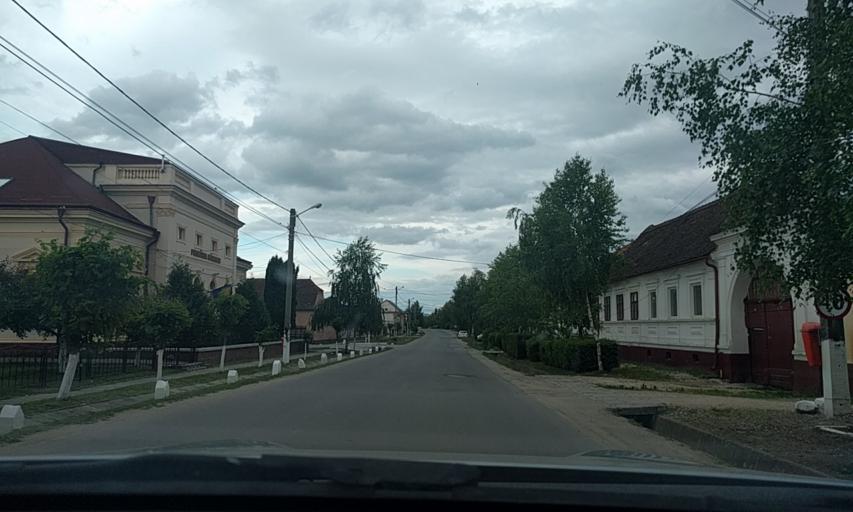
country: RO
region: Brasov
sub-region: Comuna Harman
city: Harman
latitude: 45.7138
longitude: 25.6854
